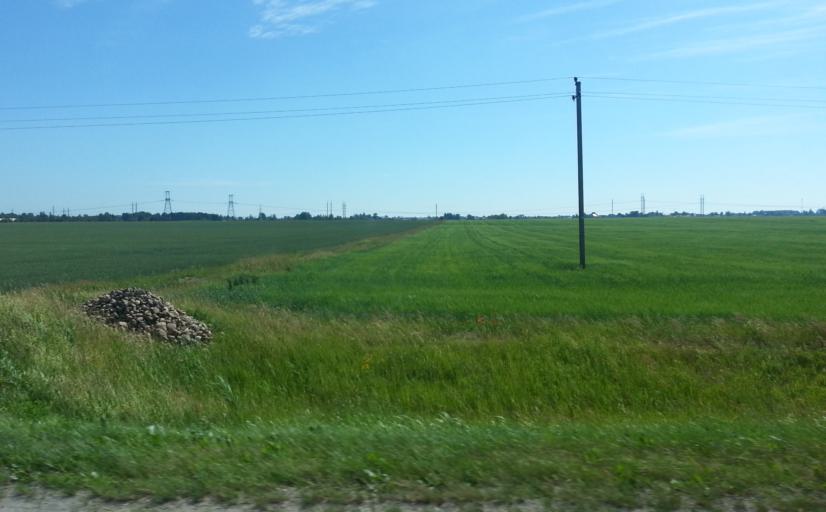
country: LT
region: Panevezys
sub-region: Panevezys City
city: Panevezys
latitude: 55.7098
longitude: 24.2702
